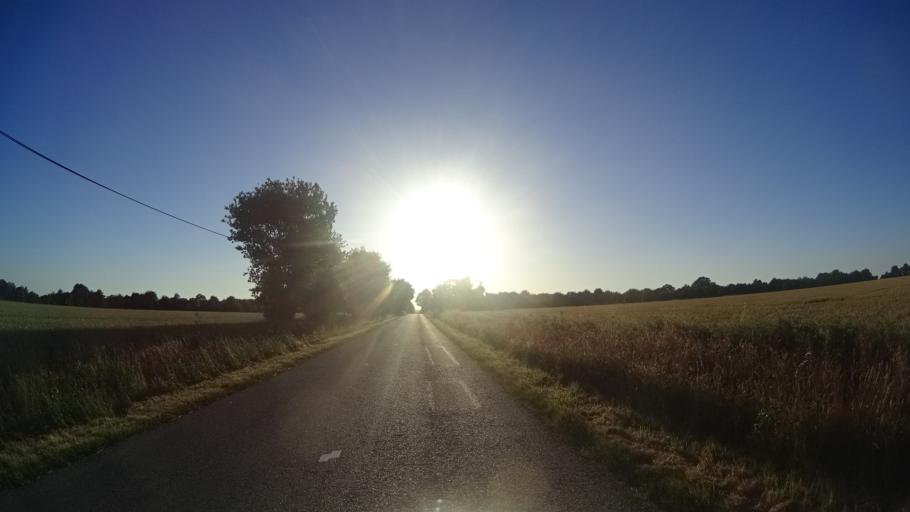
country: FR
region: Brittany
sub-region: Departement d'Ille-et-Vilaine
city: Grand-Fougeray
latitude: 47.7298
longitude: -1.7584
